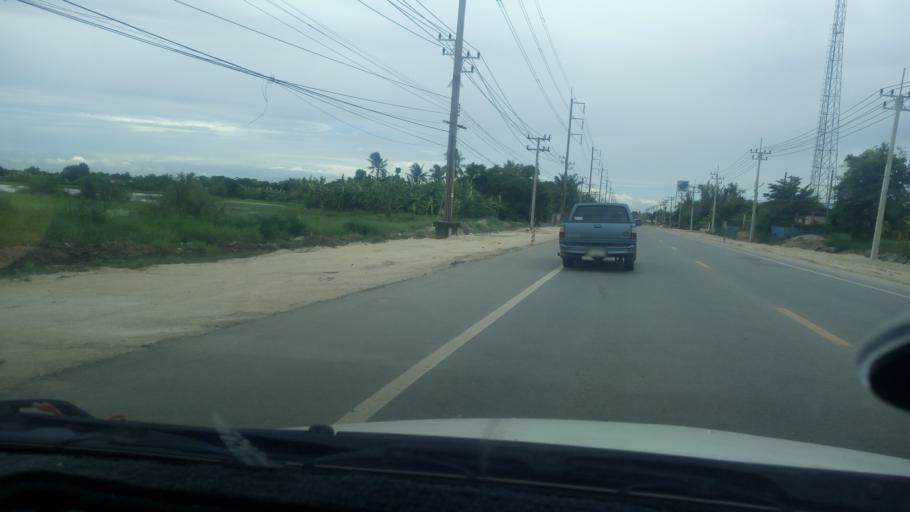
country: TH
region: Chon Buri
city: Phanat Nikhom
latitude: 13.5159
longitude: 101.1554
